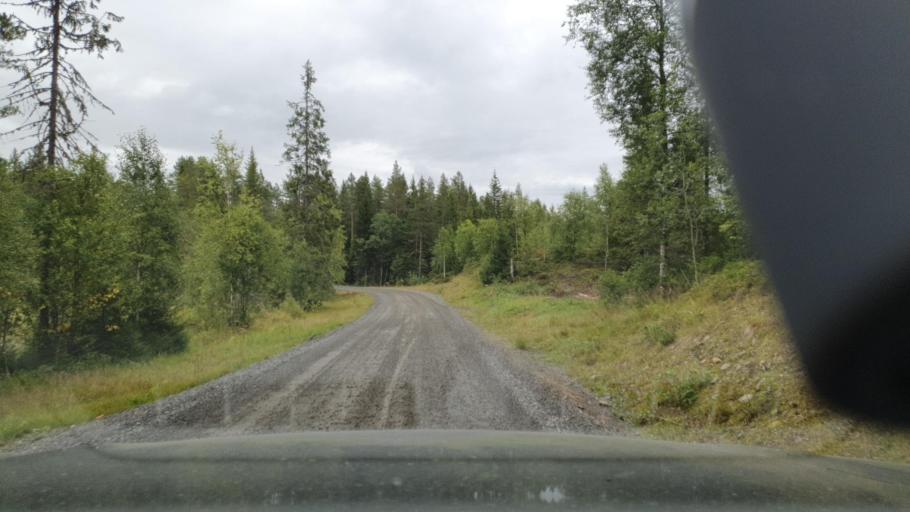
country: SE
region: Vaermland
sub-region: Torsby Kommun
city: Torsby
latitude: 60.4118
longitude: 12.6873
